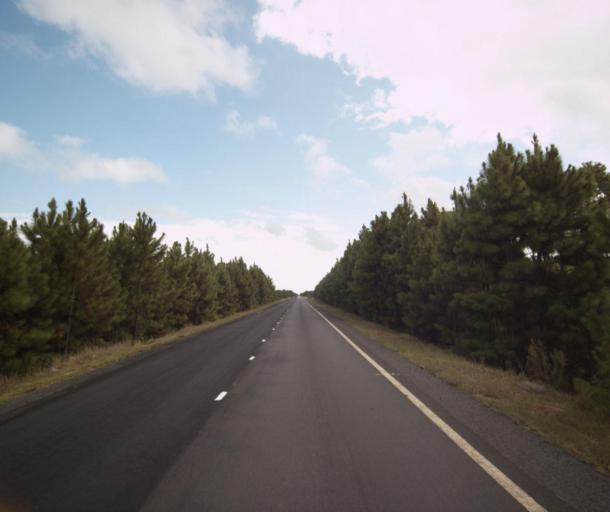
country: BR
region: Rio Grande do Sul
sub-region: Tapes
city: Tapes
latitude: -31.4172
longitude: -51.1753
